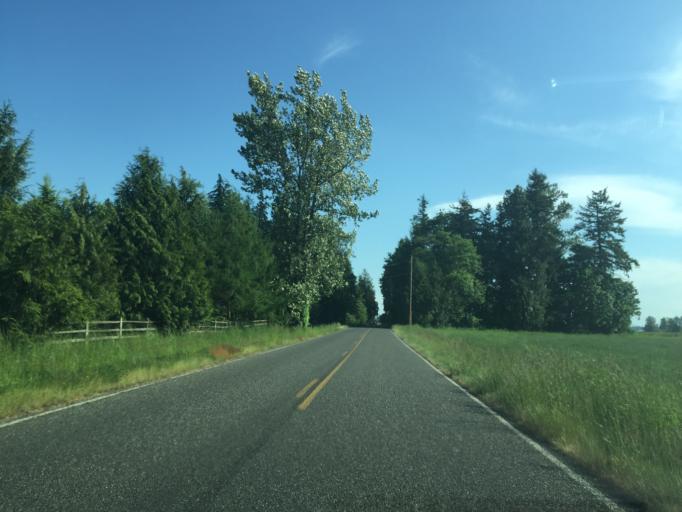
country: US
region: Washington
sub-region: Whatcom County
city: Lynden
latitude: 48.9806
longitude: -122.4628
